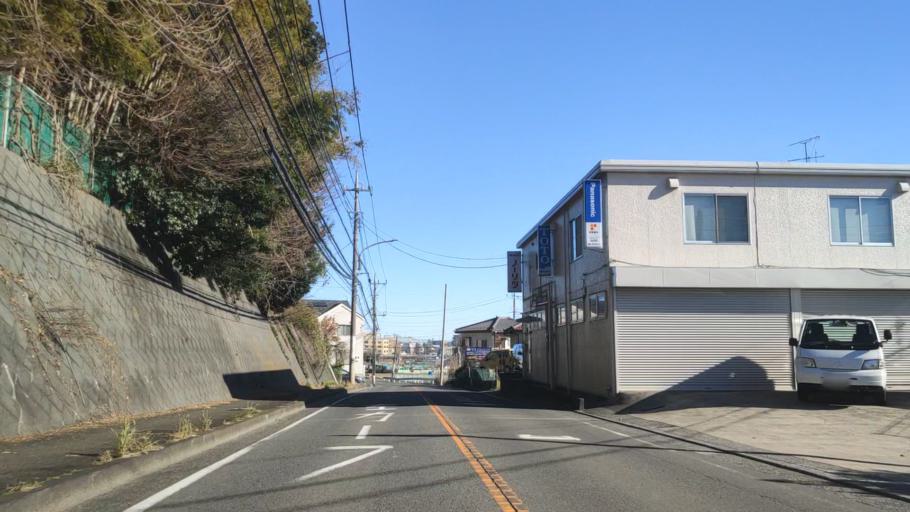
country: JP
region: Tokyo
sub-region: Machida-shi
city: Machida
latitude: 35.5191
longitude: 139.5388
